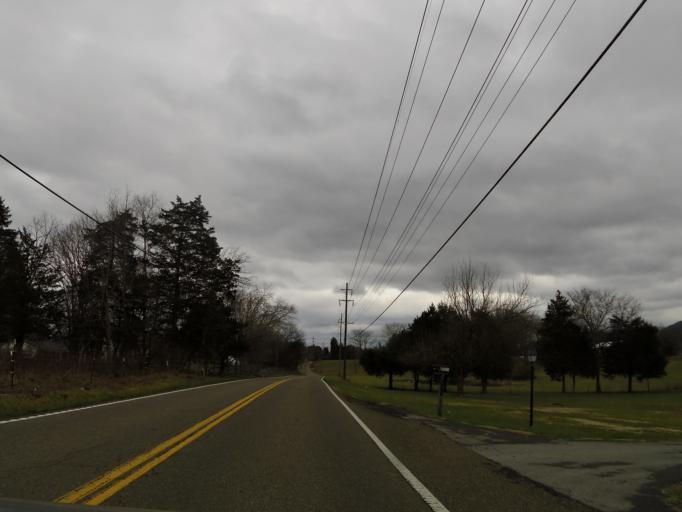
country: US
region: Tennessee
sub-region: Union County
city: Condon
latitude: 36.1349
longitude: -83.8119
